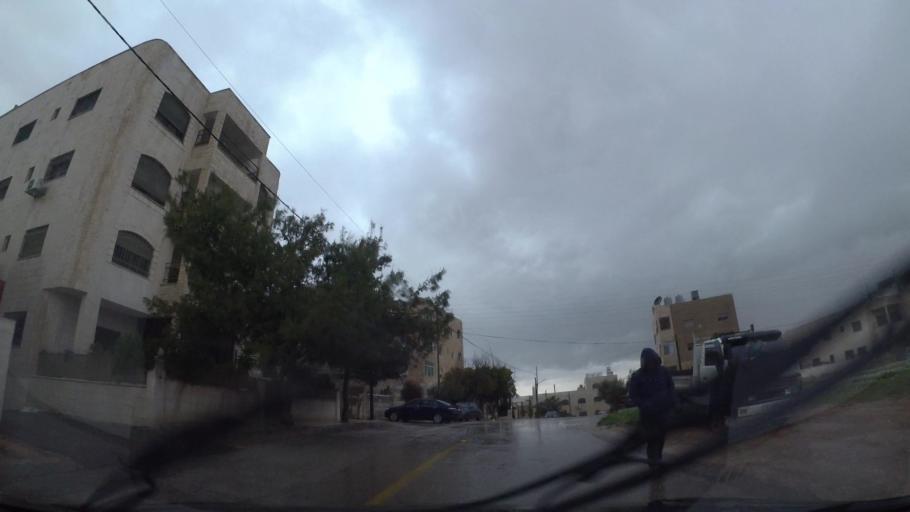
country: JO
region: Amman
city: Amman
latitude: 32.0027
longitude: 35.9586
